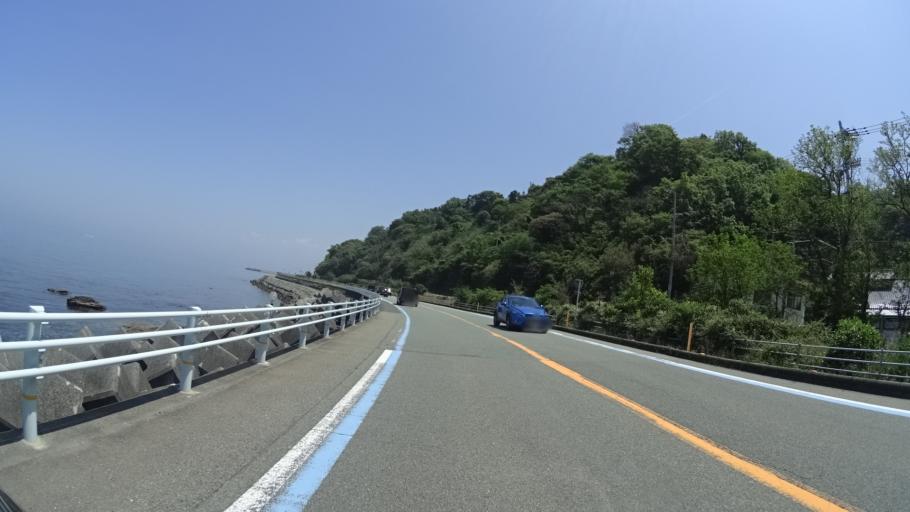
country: JP
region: Ehime
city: Ozu
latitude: 33.6289
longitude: 132.5156
